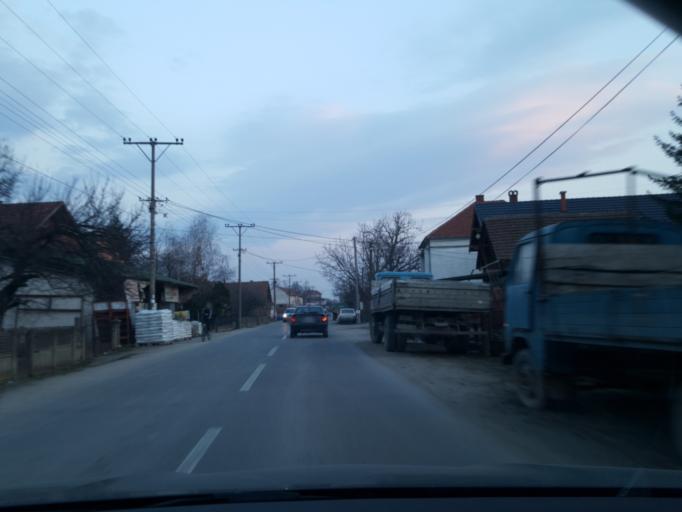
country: RS
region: Central Serbia
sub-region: Nisavski Okrug
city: Aleksinac
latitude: 43.5025
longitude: 21.7009
